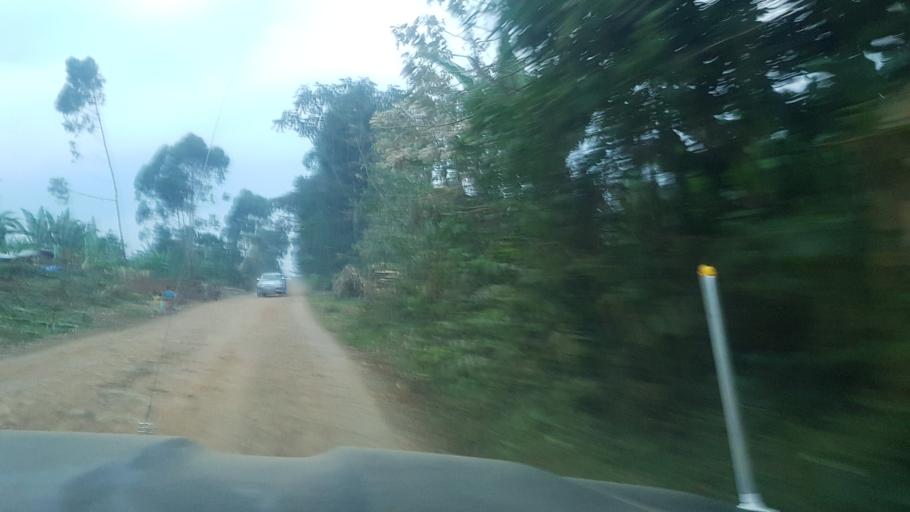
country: ET
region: Oromiya
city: Gore
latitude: 7.7672
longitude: 35.4709
